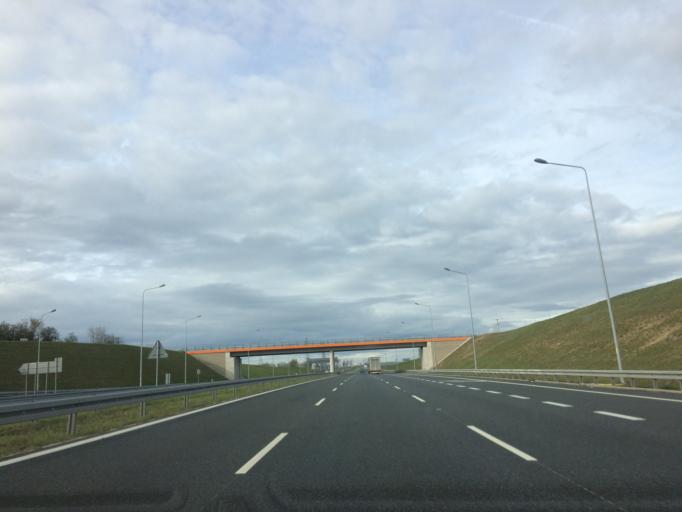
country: PL
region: Lower Silesian Voivodeship
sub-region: Legnica
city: Legnica
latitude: 51.1744
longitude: 16.0934
